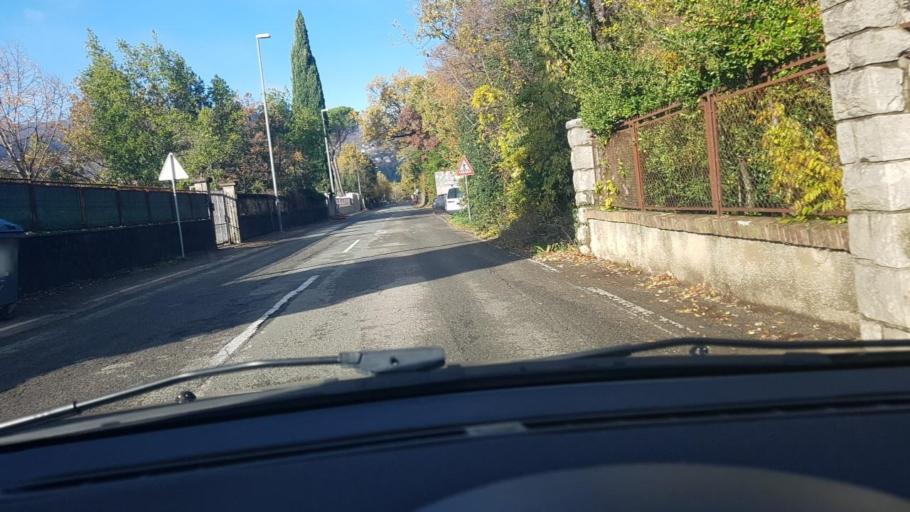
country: HR
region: Primorsko-Goranska
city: Rubesi
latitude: 45.3486
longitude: 14.3469
